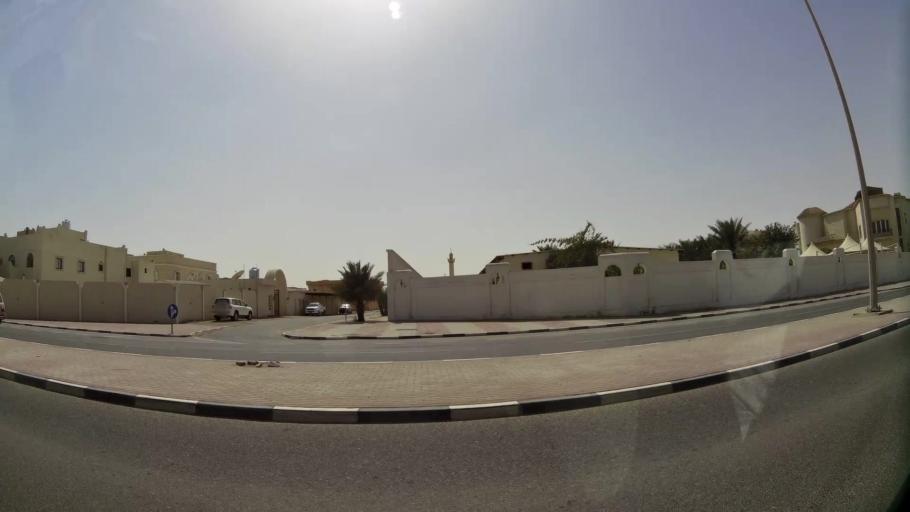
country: QA
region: Baladiyat Umm Salal
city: Umm Salal Muhammad
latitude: 25.3745
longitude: 51.4321
